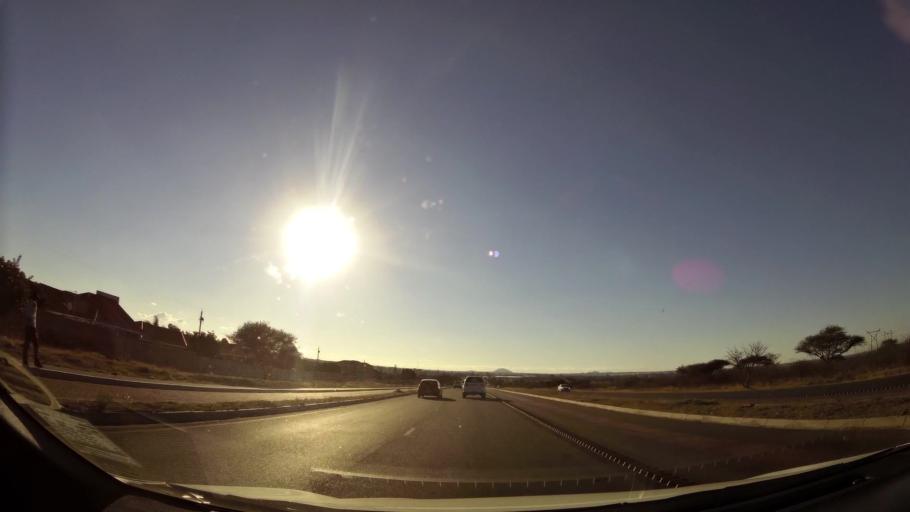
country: ZA
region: Limpopo
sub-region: Capricorn District Municipality
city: Polokwane
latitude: -23.8615
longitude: 29.4056
